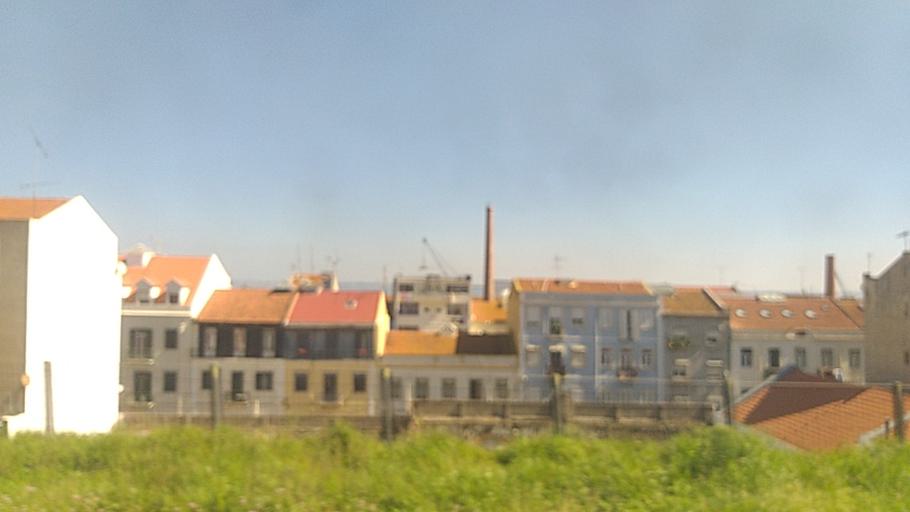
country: PT
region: Lisbon
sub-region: Lisbon
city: Lisbon
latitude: 38.7389
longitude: -9.1059
